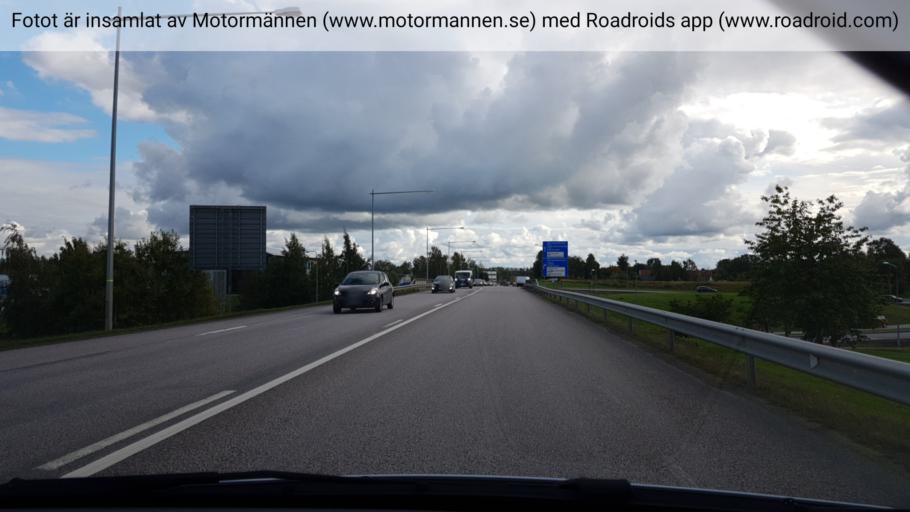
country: SE
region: Vaestra Goetaland
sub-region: Skovde Kommun
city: Skoevde
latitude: 58.3950
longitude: 13.8733
